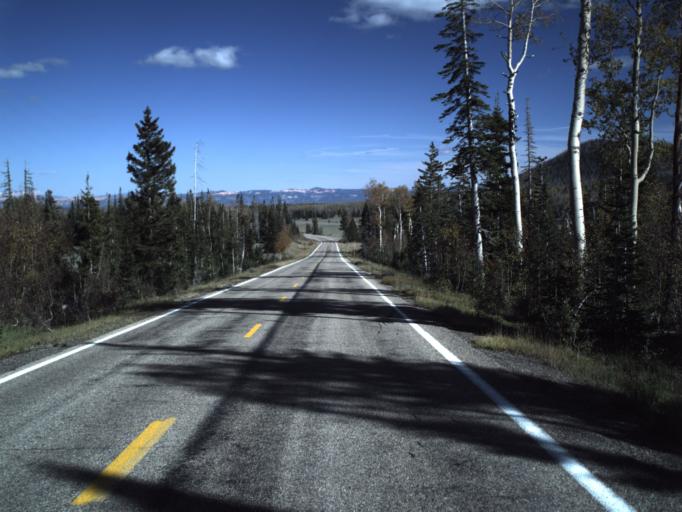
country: US
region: Utah
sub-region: Iron County
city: Parowan
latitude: 37.6514
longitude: -112.7955
